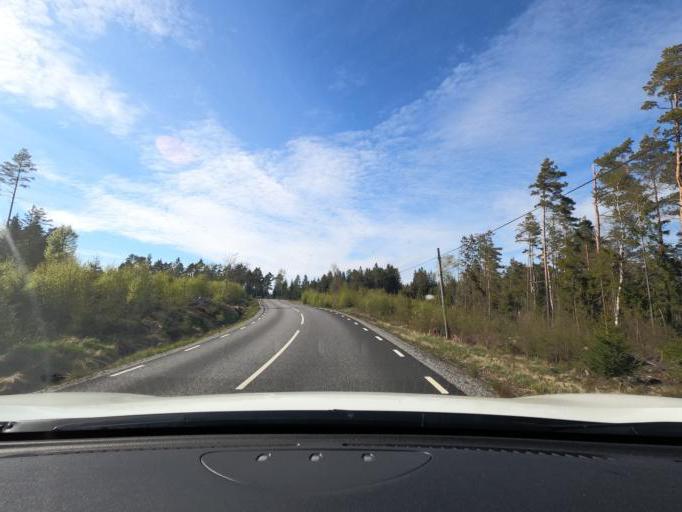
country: SE
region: Vaestra Goetaland
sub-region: Harryda Kommun
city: Landvetter
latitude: 57.6404
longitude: 12.2554
